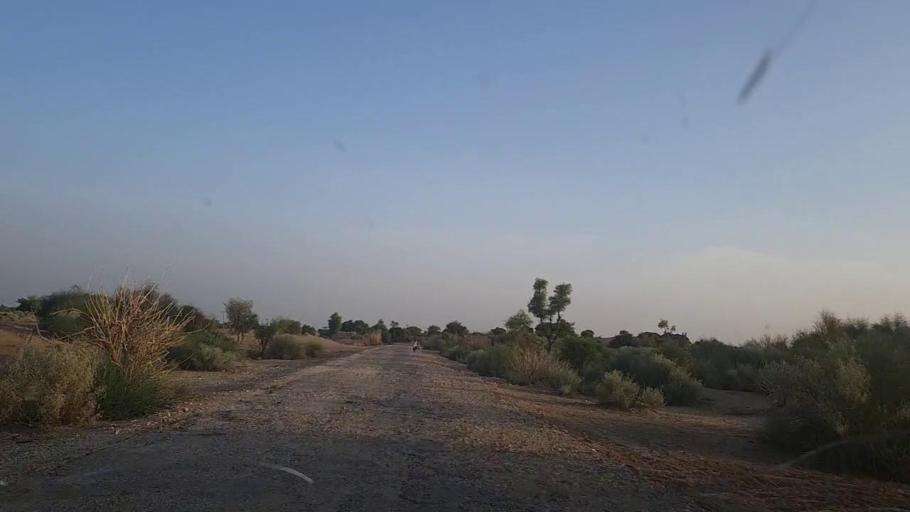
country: PK
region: Sindh
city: Khanpur
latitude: 27.6274
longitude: 69.4445
